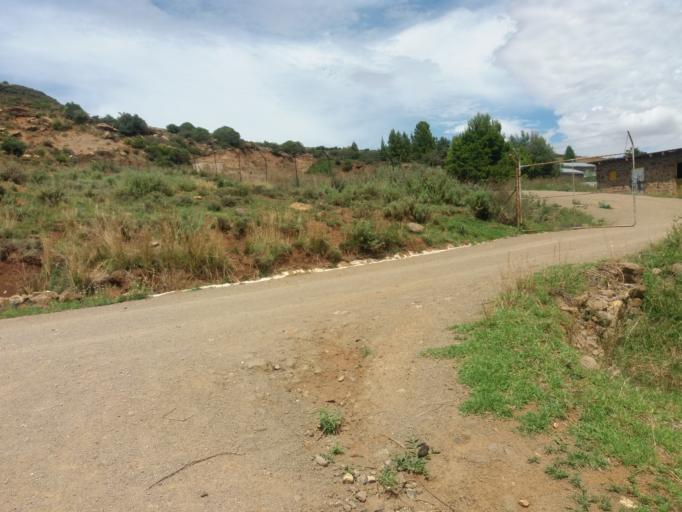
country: LS
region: Quthing
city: Quthing
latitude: -30.4120
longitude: 27.6950
